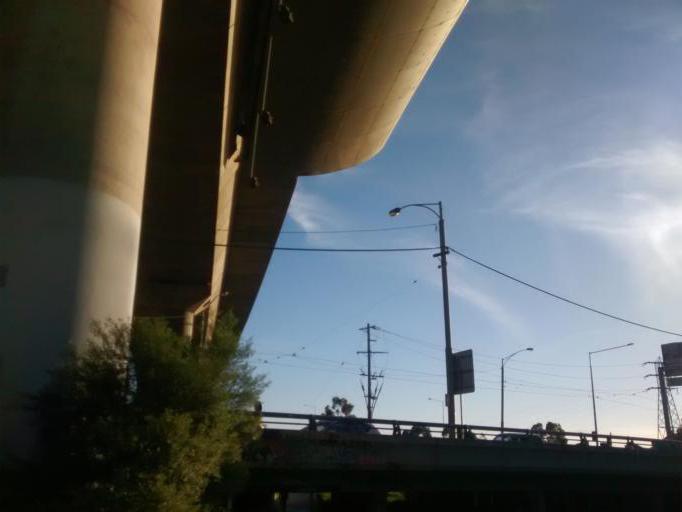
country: AU
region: Victoria
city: Kensington
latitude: -37.7886
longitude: 144.9381
